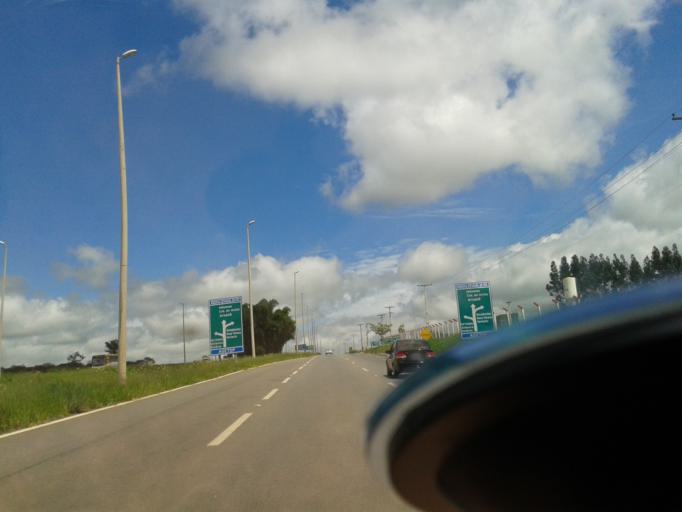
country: BR
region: Goias
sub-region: Goianira
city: Goianira
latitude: -16.4677
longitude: -49.4388
